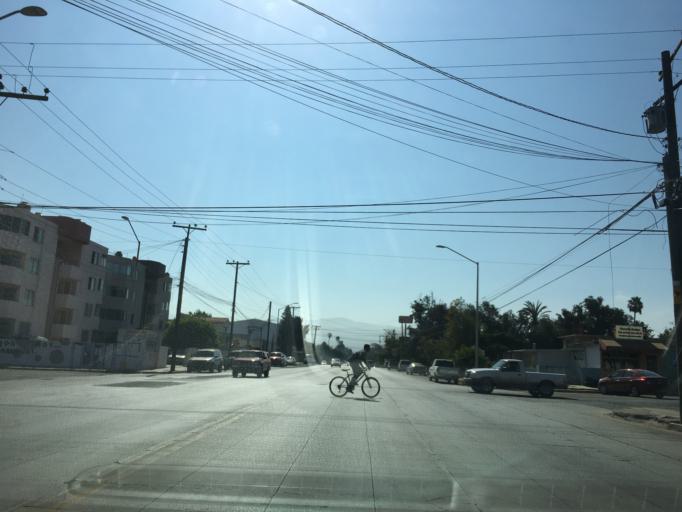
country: MX
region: Baja California
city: Ensenada
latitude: 31.8622
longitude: -116.6145
